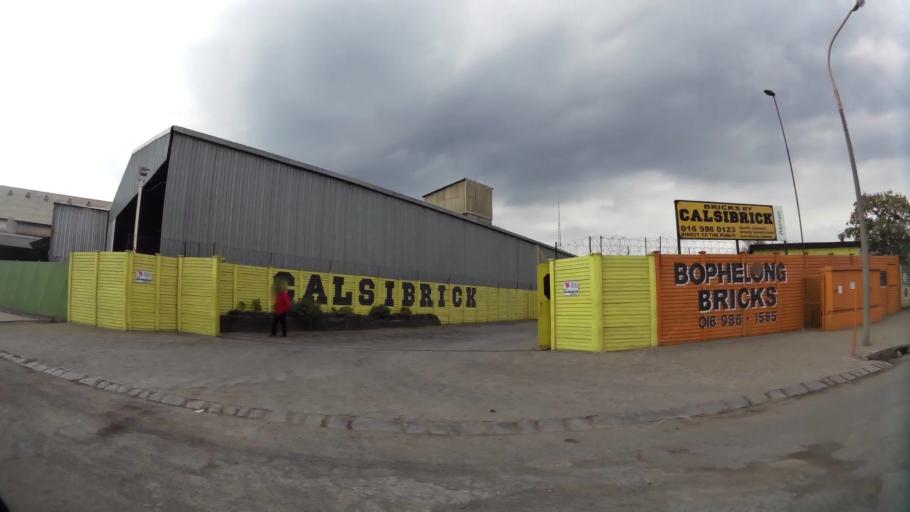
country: ZA
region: Gauteng
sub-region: Sedibeng District Municipality
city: Vanderbijlpark
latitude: -26.6881
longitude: 27.8019
